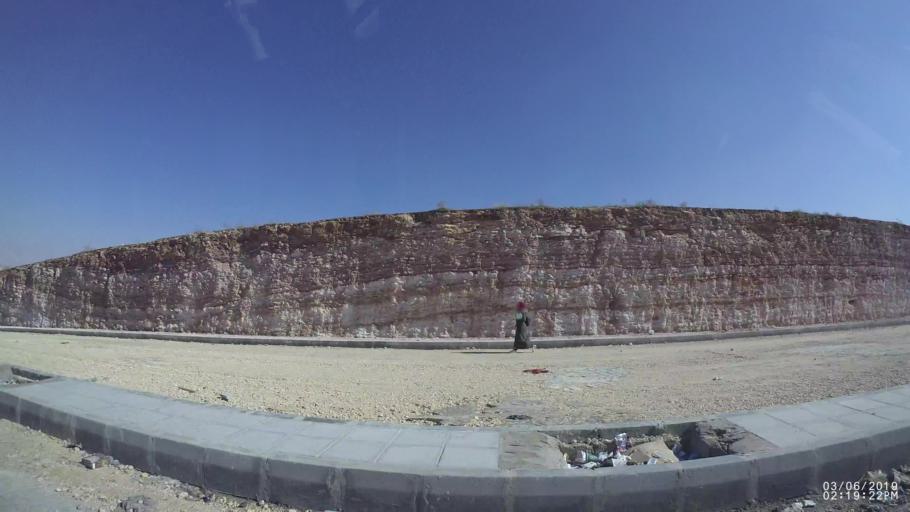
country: JO
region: Zarqa
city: Russeifa
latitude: 32.0369
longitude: 36.0482
